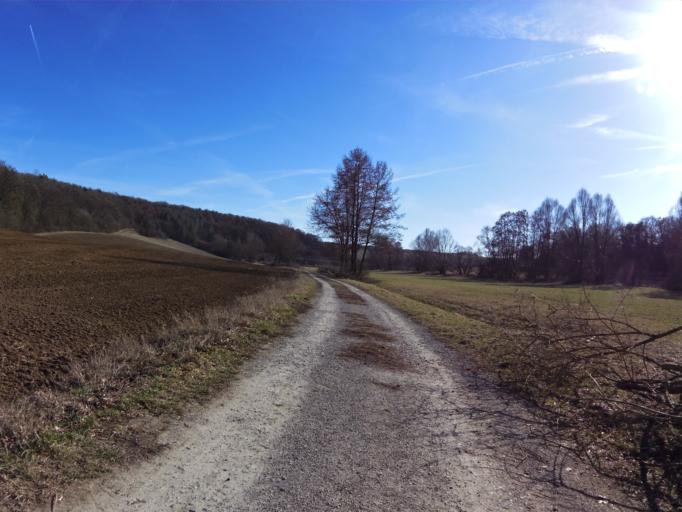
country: DE
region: Bavaria
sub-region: Regierungsbezirk Unterfranken
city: Rimpar
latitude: 49.8553
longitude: 9.9817
